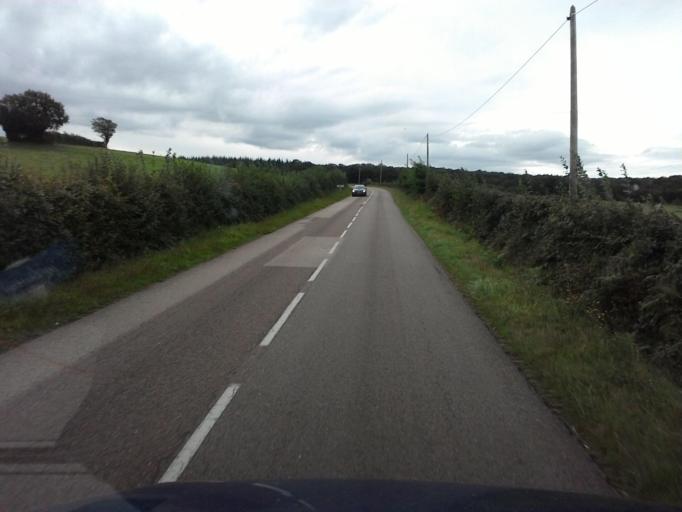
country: FR
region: Bourgogne
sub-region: Departement de la Nievre
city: Chateau-Chinon(Ville)
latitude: 47.1220
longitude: 3.8910
